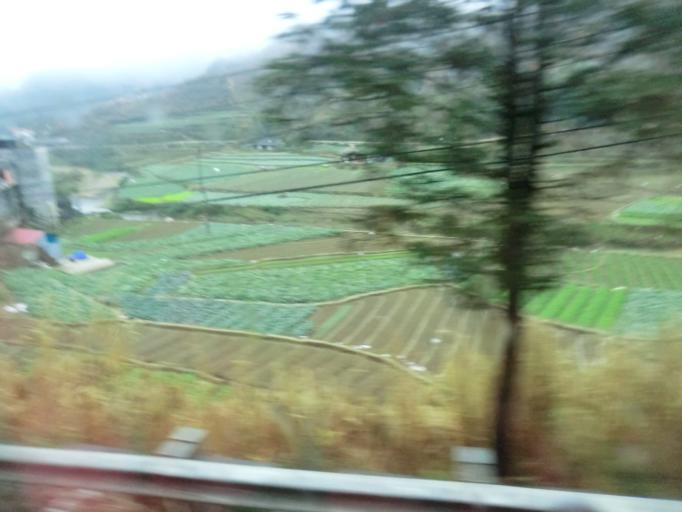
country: VN
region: Lao Cai
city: Sa Pa
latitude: 22.3652
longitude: 103.8667
